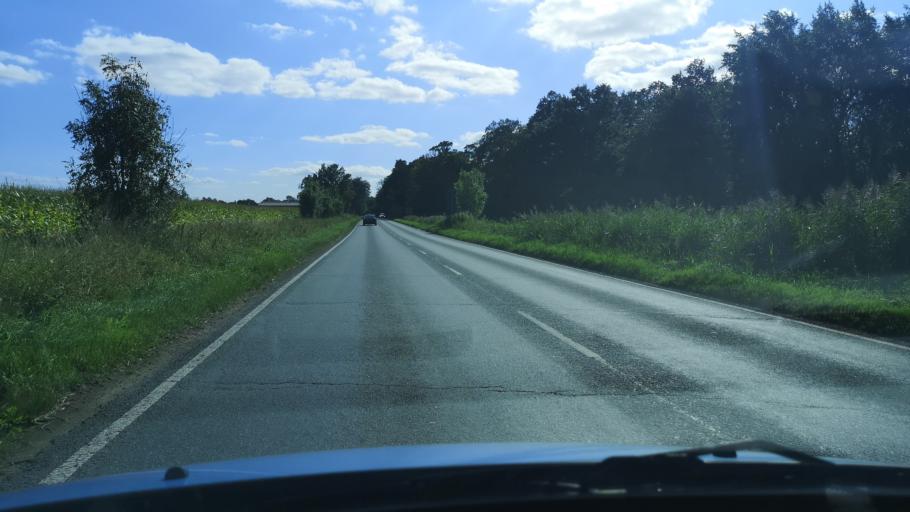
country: GB
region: England
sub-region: North Lincolnshire
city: Crowle
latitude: 53.5850
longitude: -0.8195
